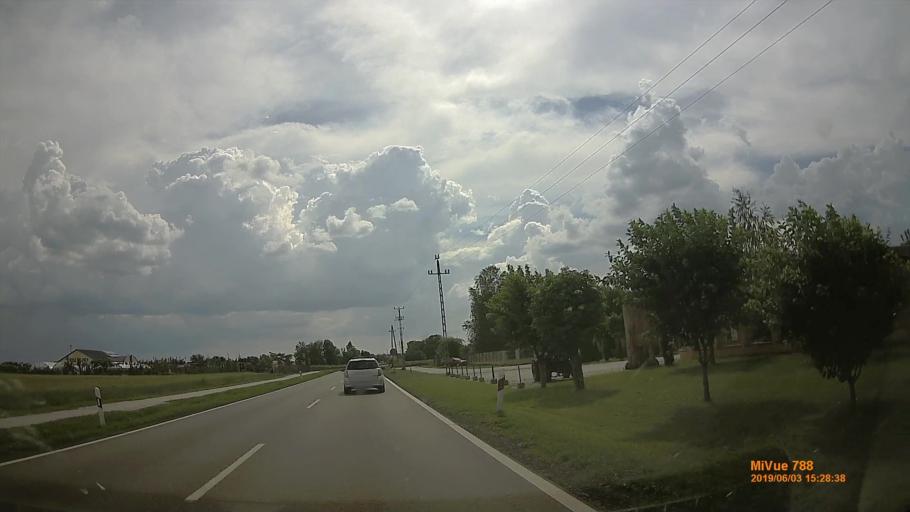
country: HU
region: Bacs-Kiskun
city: Soltvadkert
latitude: 46.5894
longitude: 19.4029
